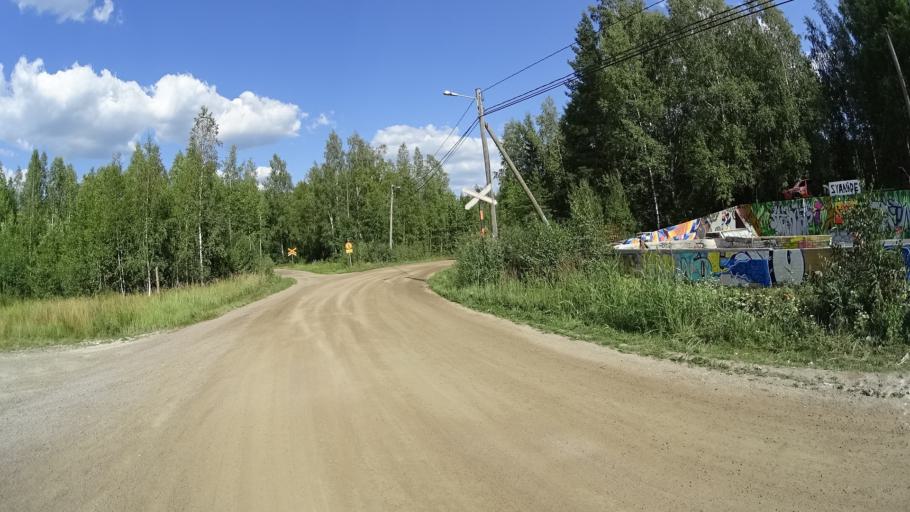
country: FI
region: Uusimaa
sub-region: Porvoo
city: Porvoo
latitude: 60.3987
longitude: 25.6403
